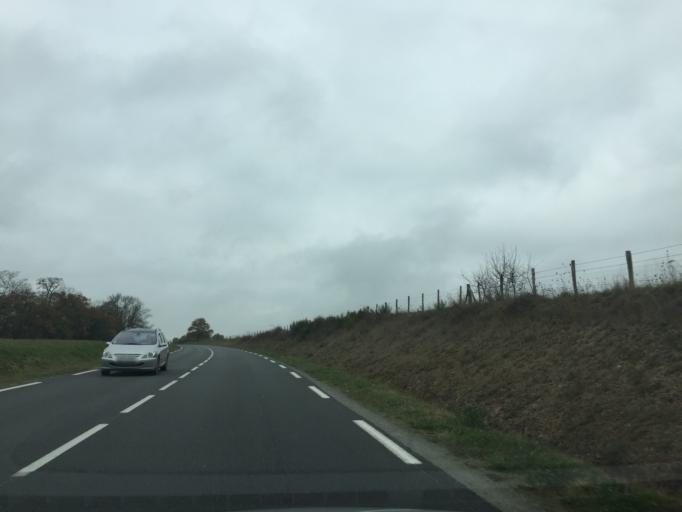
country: FR
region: Limousin
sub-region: Departement de la Creuse
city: Gouzon
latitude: 46.1479
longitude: 2.2052
